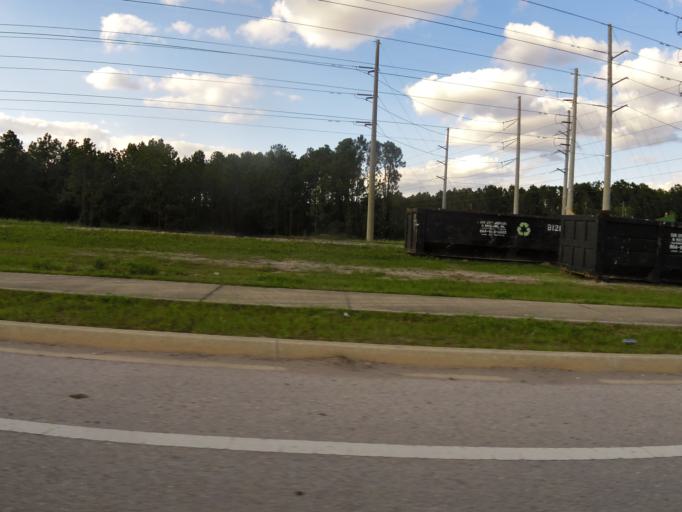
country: US
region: Florida
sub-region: Duval County
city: Jacksonville Beach
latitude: 30.2646
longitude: -81.5226
